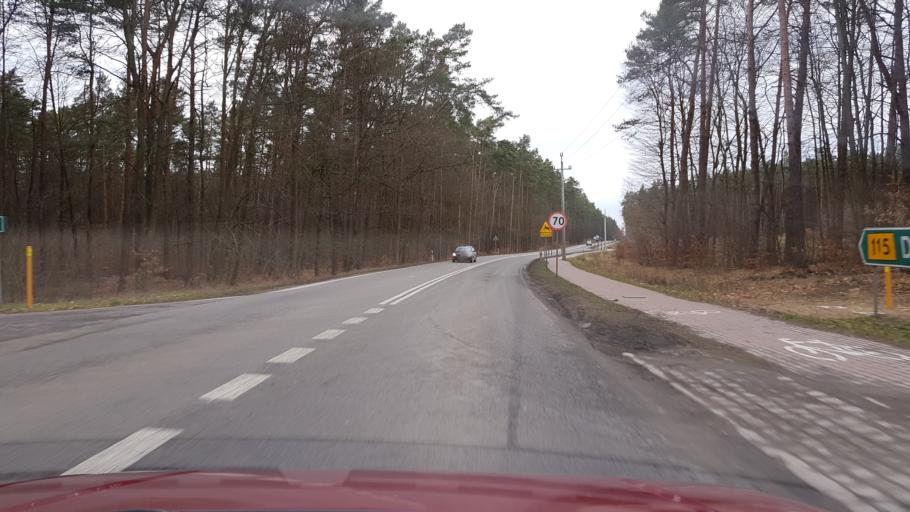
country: PL
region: West Pomeranian Voivodeship
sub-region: Powiat policki
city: Dobra
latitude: 53.5184
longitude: 14.4706
